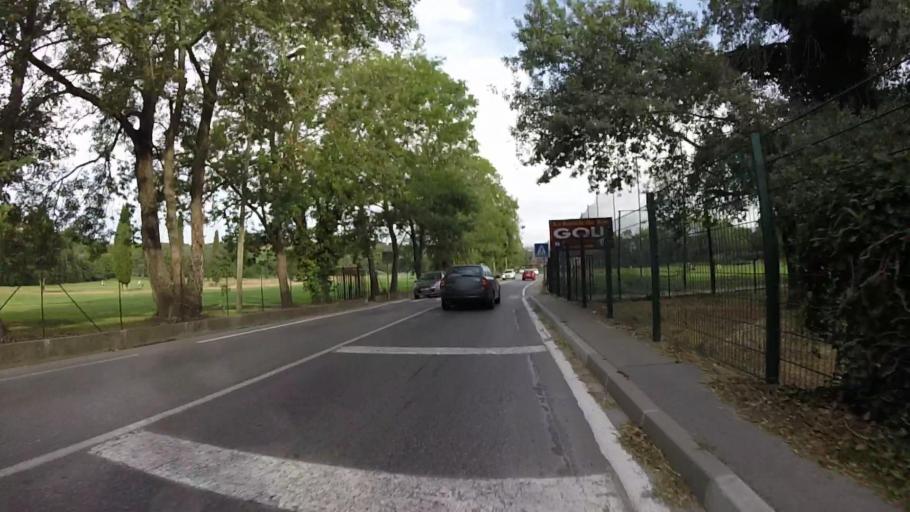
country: FR
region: Provence-Alpes-Cote d'Azur
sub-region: Departement des Alpes-Maritimes
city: Biot
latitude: 43.6157
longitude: 7.1074
